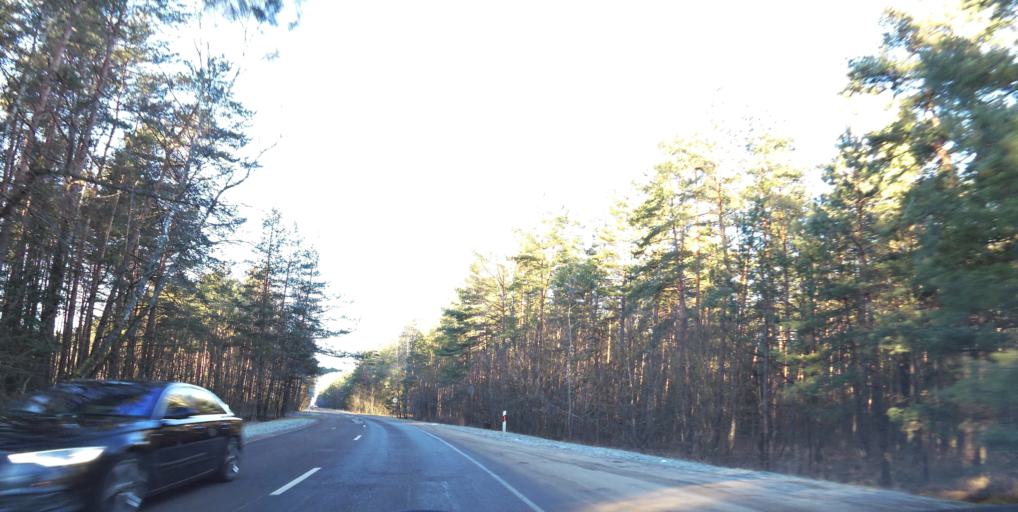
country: LT
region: Vilnius County
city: Lazdynai
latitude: 54.6422
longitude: 25.1742
